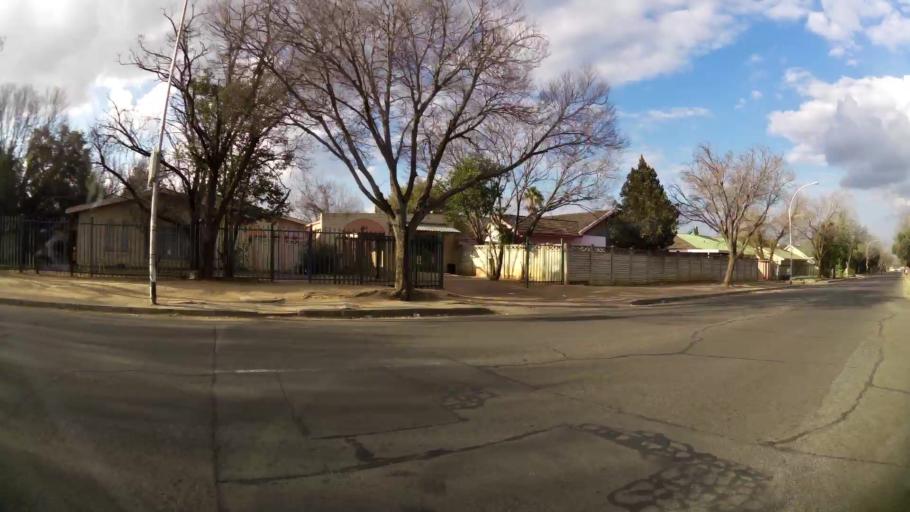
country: ZA
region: Orange Free State
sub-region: Mangaung Metropolitan Municipality
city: Bloemfontein
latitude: -29.1049
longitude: 26.1951
